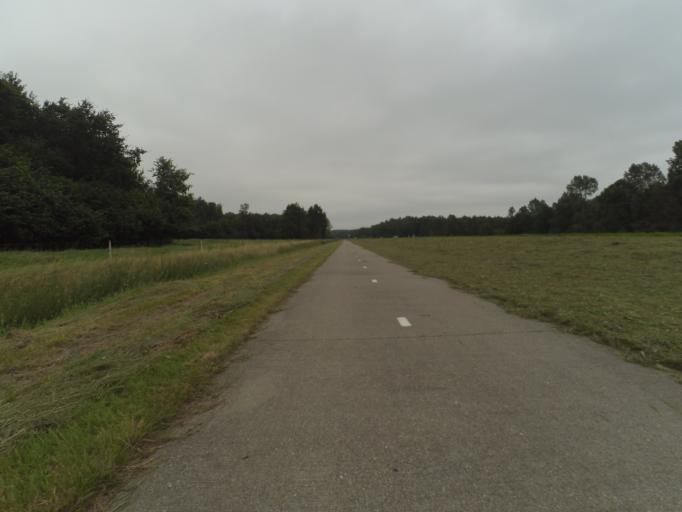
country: NL
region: Flevoland
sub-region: Gemeente Zeewolde
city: Zeewolde
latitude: 52.4141
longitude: 5.4989
